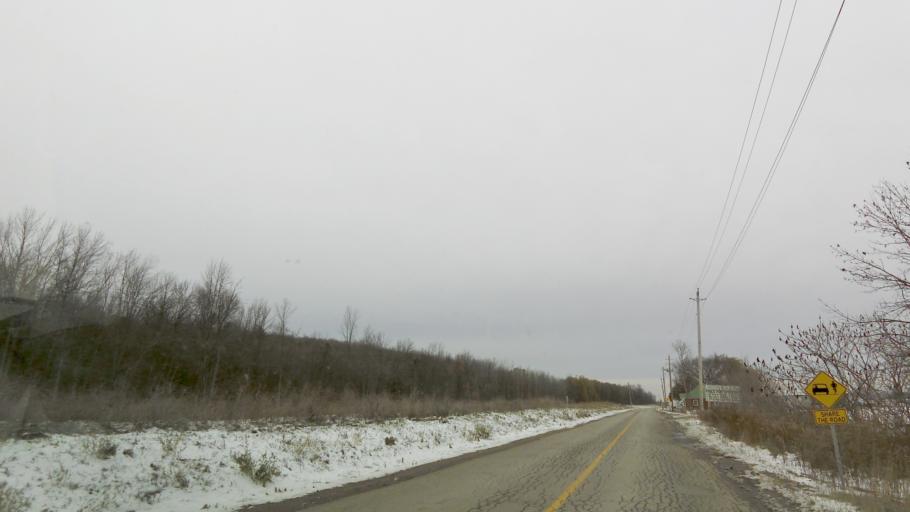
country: CA
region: Ontario
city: Bradford West Gwillimbury
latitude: 44.0544
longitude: -79.6060
